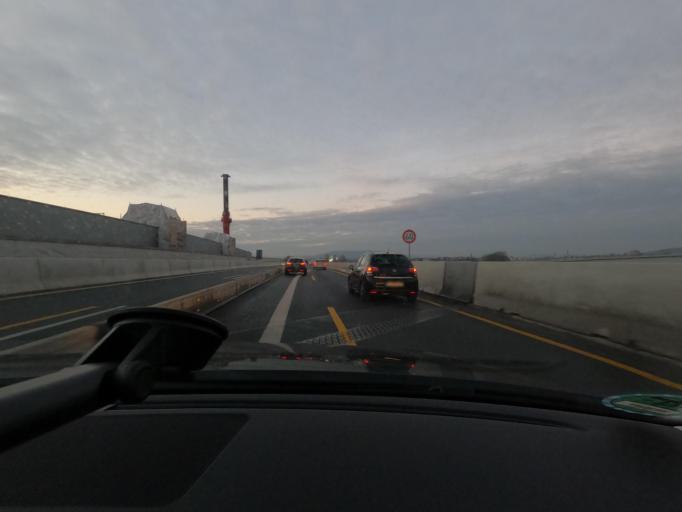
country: DE
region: Bavaria
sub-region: Upper Franconia
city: Kemmern
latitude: 49.9581
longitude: 10.8859
